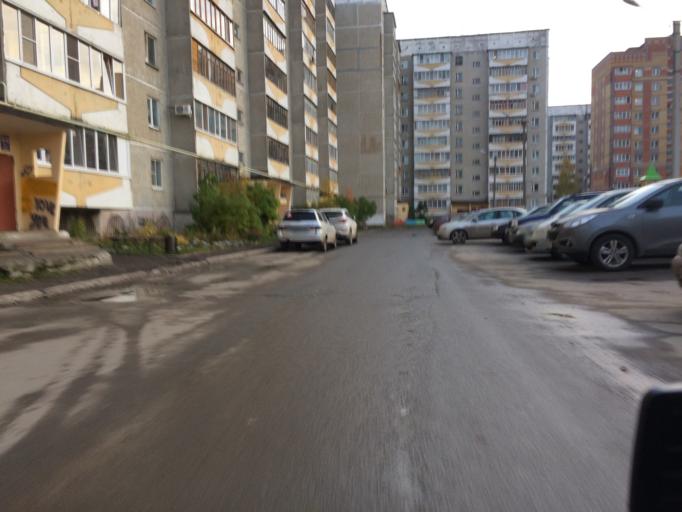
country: RU
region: Mariy-El
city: Yoshkar-Ola
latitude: 56.6326
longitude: 47.9291
